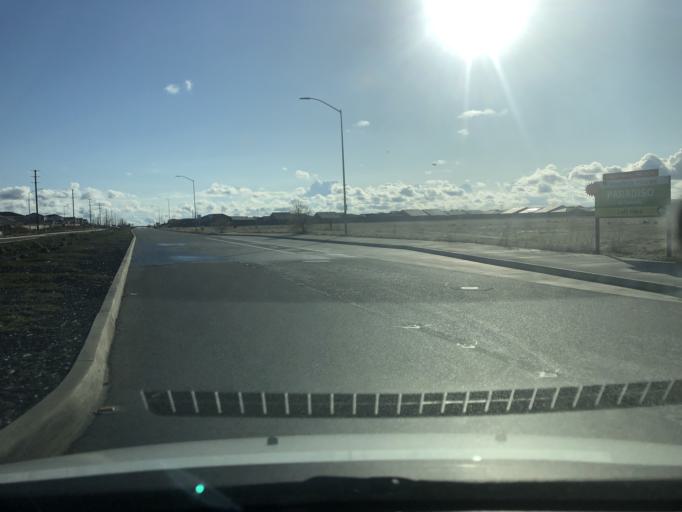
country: US
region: California
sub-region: Sacramento County
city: Antelope
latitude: 38.7752
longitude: -121.3852
